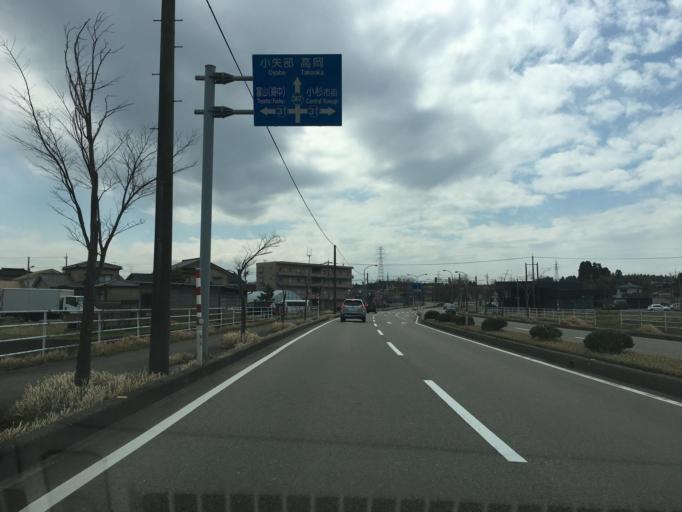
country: JP
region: Toyama
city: Kuragaki-kosugi
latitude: 36.7008
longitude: 137.1135
